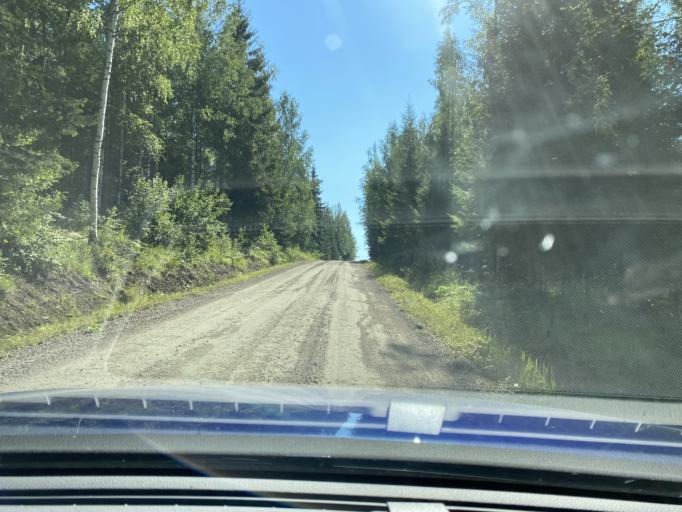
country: FI
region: Central Finland
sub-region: Jyvaeskylae
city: Korpilahti
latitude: 61.8728
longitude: 25.4158
